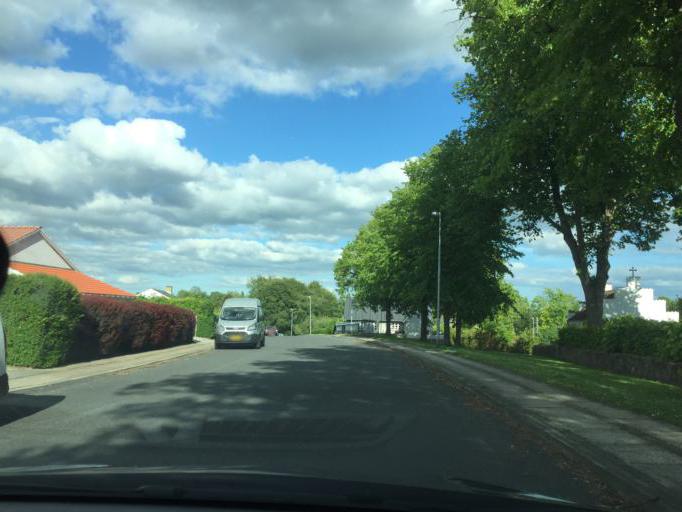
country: DK
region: South Denmark
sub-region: Odense Kommune
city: Bellinge
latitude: 55.3337
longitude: 10.3134
